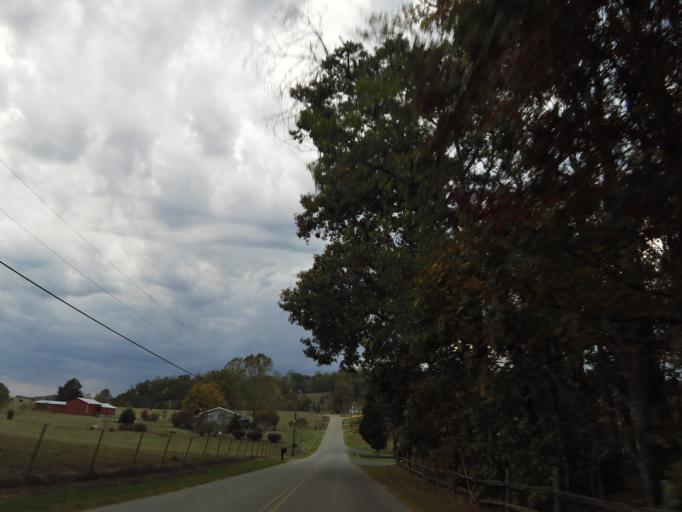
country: US
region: Tennessee
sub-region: Blount County
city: Louisville
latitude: 35.7837
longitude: -84.0571
